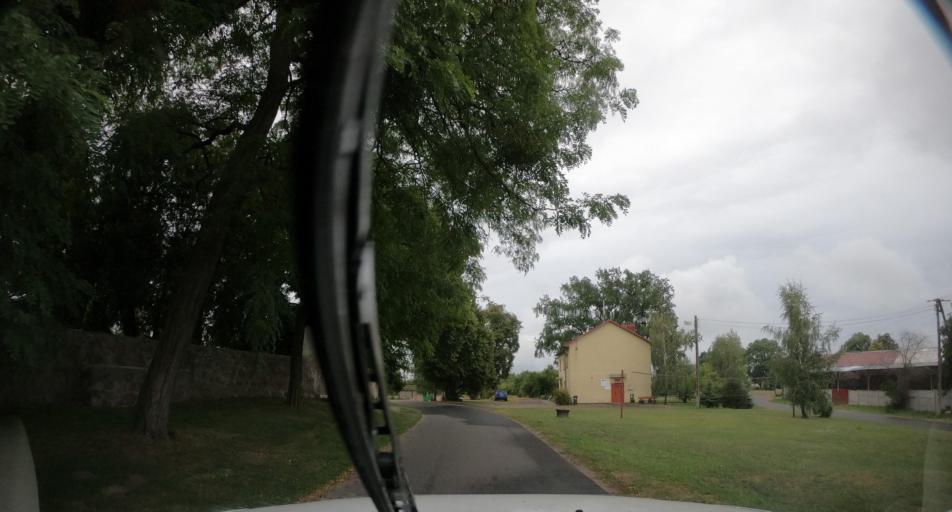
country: PL
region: West Pomeranian Voivodeship
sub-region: Powiat stargardzki
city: Suchan
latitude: 53.2690
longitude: 15.4051
